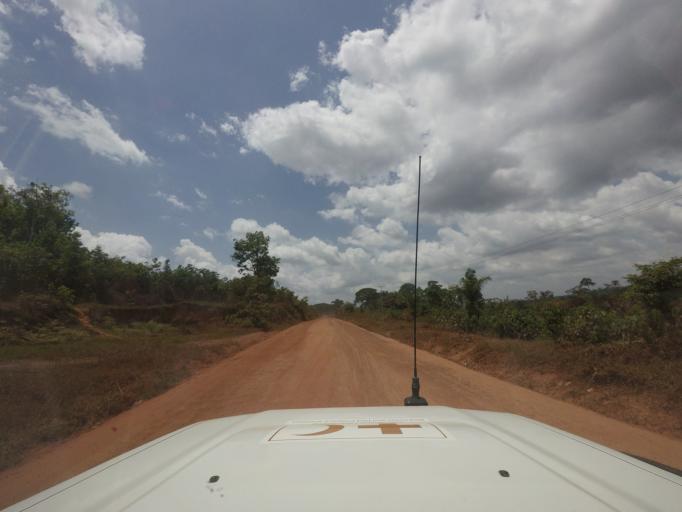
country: LR
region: Nimba
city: Sanniquellie
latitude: 7.2348
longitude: -8.9605
